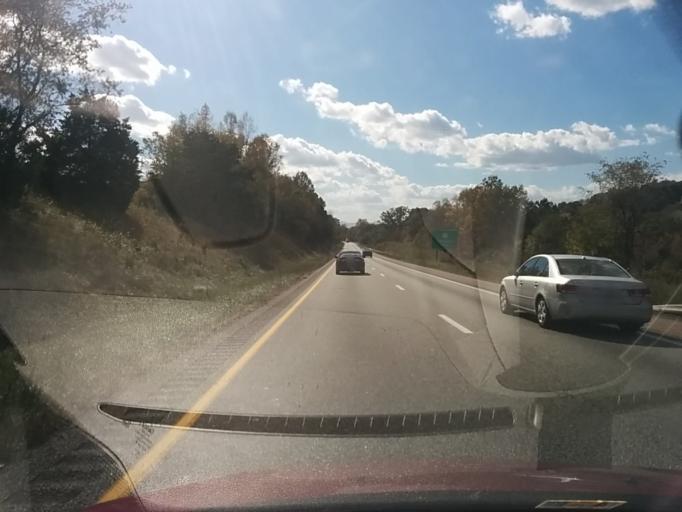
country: US
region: Virginia
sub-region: Rockbridge County
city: East Lexington
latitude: 37.8549
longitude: -79.3546
